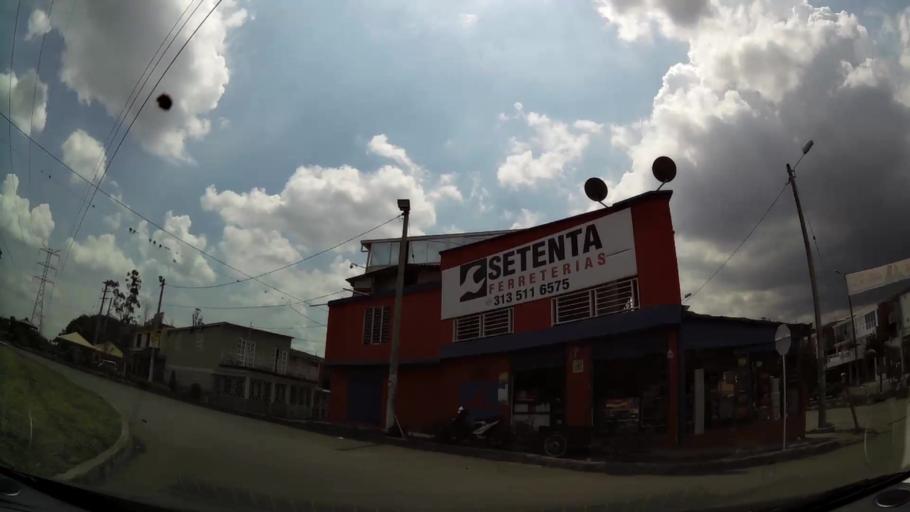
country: CO
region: Valle del Cauca
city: Cali
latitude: 3.4571
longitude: -76.4679
